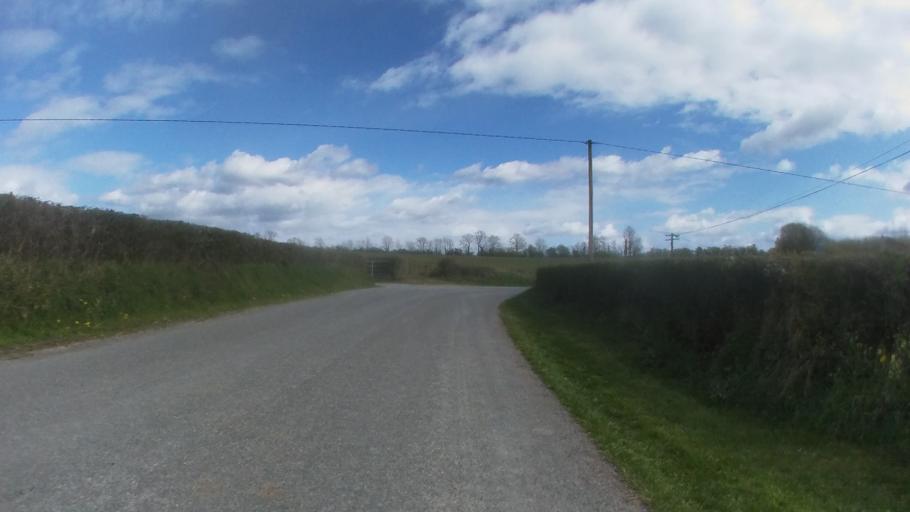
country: IE
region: Leinster
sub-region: Kilkenny
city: Kilkenny
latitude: 52.7149
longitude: -7.2233
